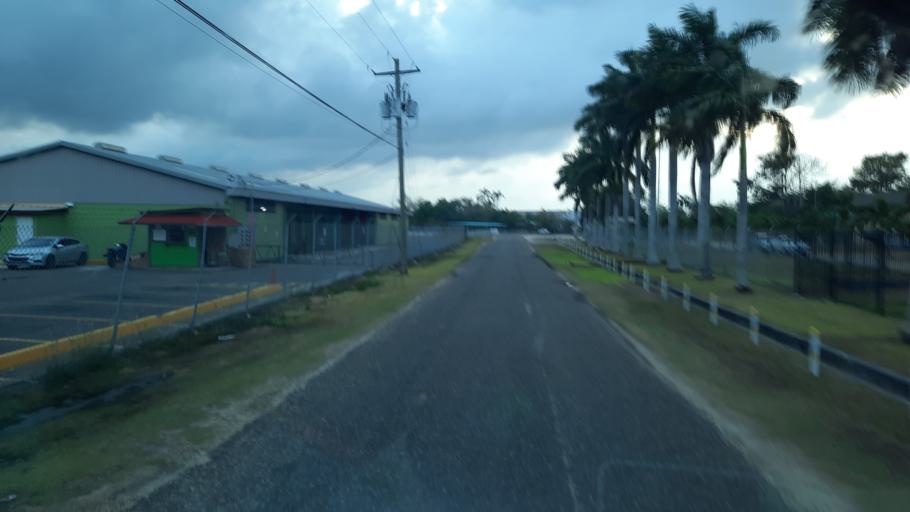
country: BZ
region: Belize
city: Belize City
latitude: 17.5427
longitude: -88.3007
